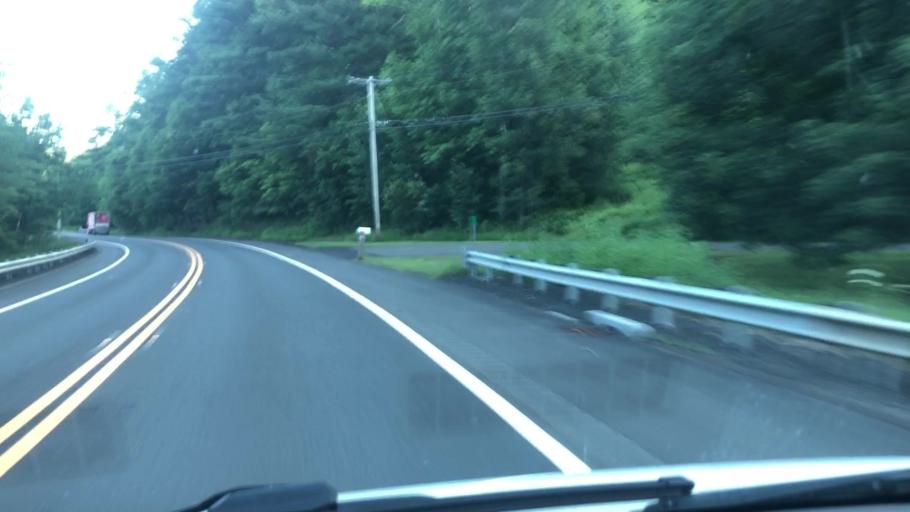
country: US
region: Massachusetts
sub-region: Hampshire County
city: Chesterfield
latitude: 42.4530
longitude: -72.8231
